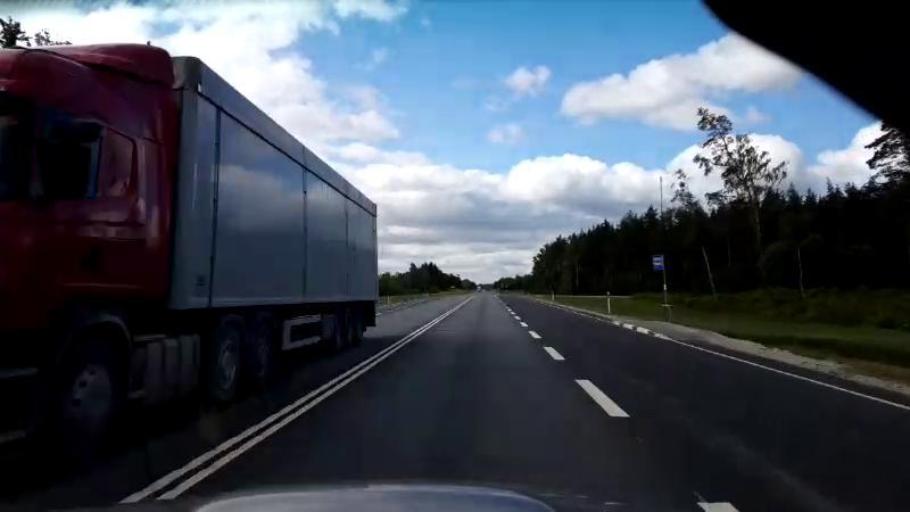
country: EE
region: Harju
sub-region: Nissi vald
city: Riisipere
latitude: 59.0606
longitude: 24.4484
